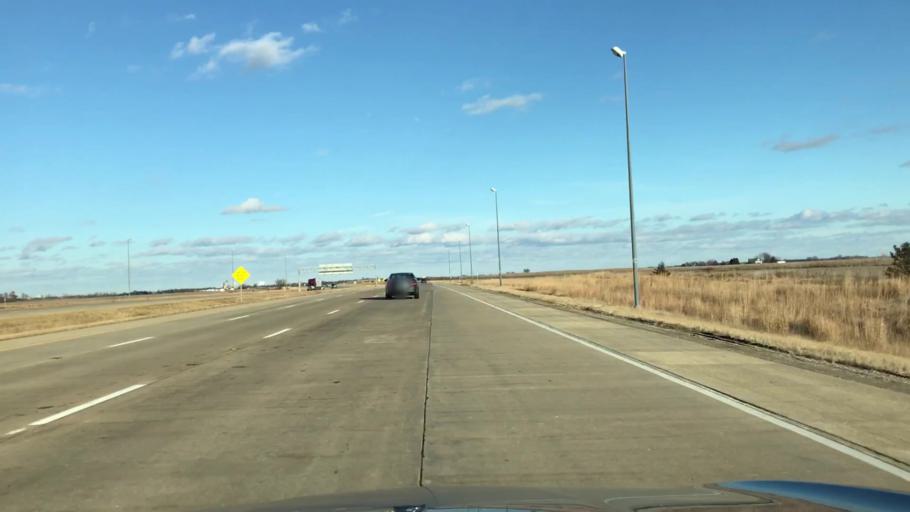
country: US
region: Illinois
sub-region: McLean County
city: Normal
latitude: 40.5387
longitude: -88.9409
